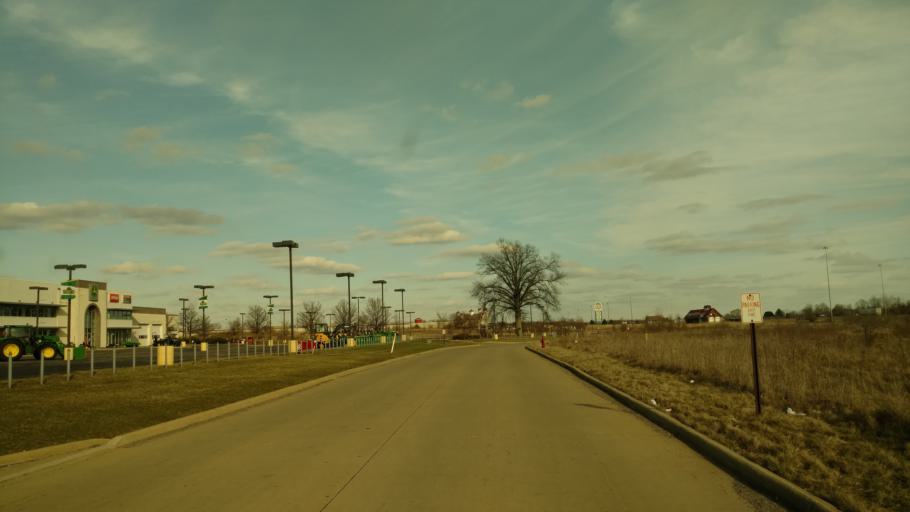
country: US
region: Ohio
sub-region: Medina County
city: Lodi
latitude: 40.9994
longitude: -81.9940
